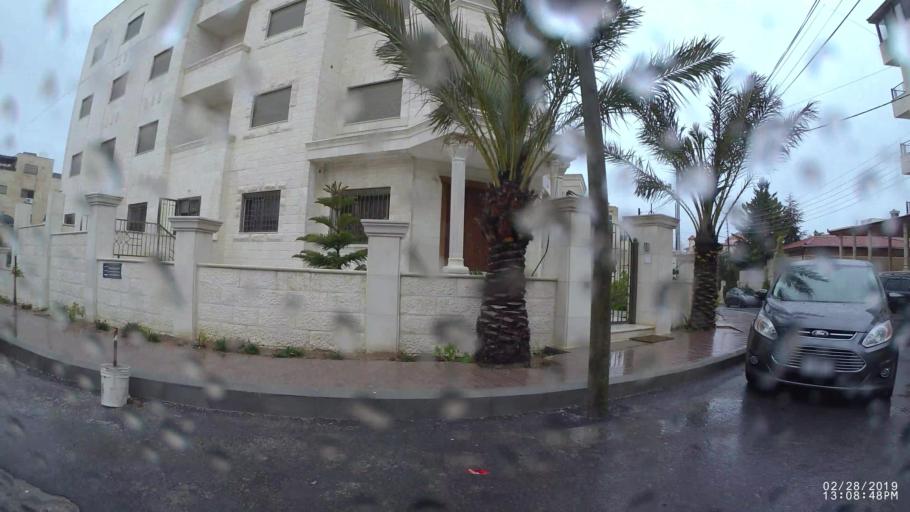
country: JO
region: Amman
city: Al Jubayhah
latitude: 32.0229
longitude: 35.8833
